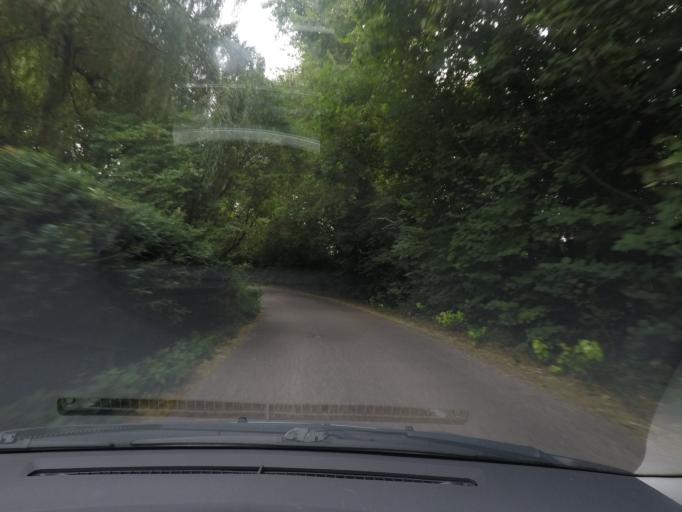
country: GB
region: England
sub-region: Wiltshire
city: Woodborough
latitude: 51.3291
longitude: -1.8036
